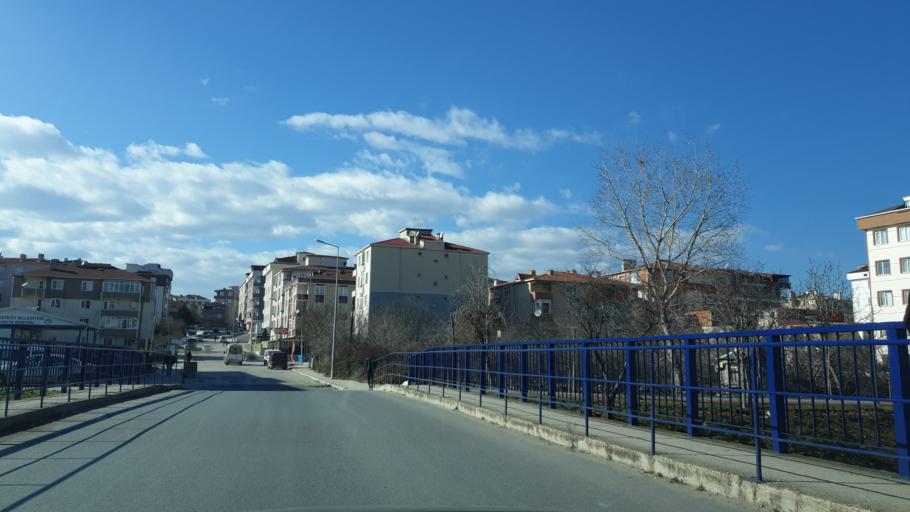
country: TR
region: Tekirdag
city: Cerkezkoey
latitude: 41.2876
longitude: 28.0068
